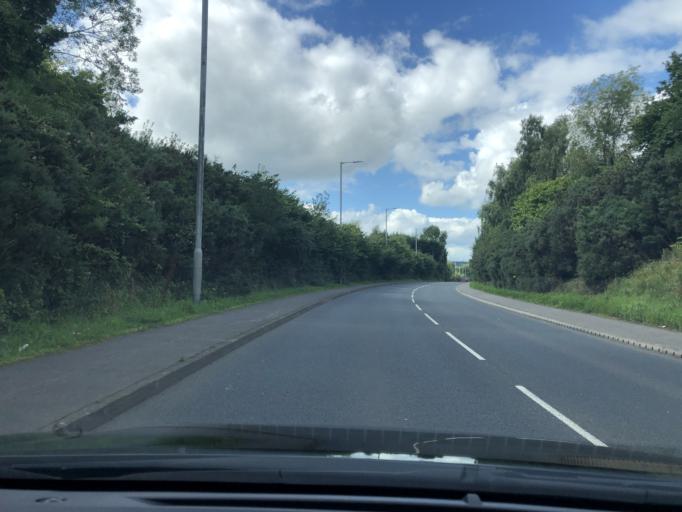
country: GB
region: Northern Ireland
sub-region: Ards District
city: Newtownards
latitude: 54.5847
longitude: -5.7113
